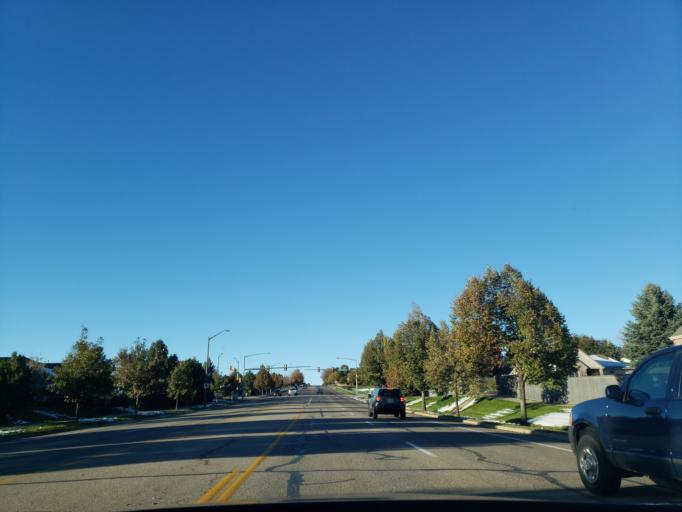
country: US
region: Colorado
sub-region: Larimer County
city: Fort Collins
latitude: 40.5079
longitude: -105.0581
